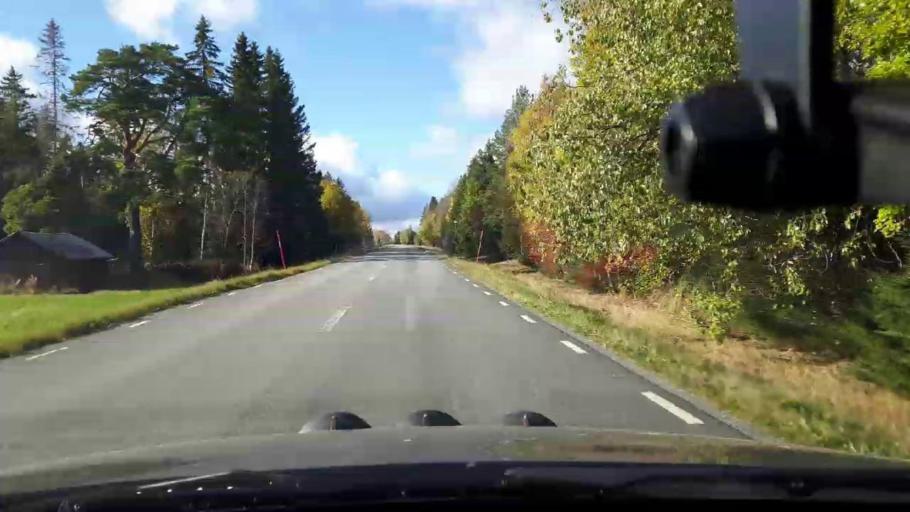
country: SE
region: Jaemtland
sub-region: Bergs Kommun
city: Hoverberg
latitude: 62.9928
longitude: 14.4173
